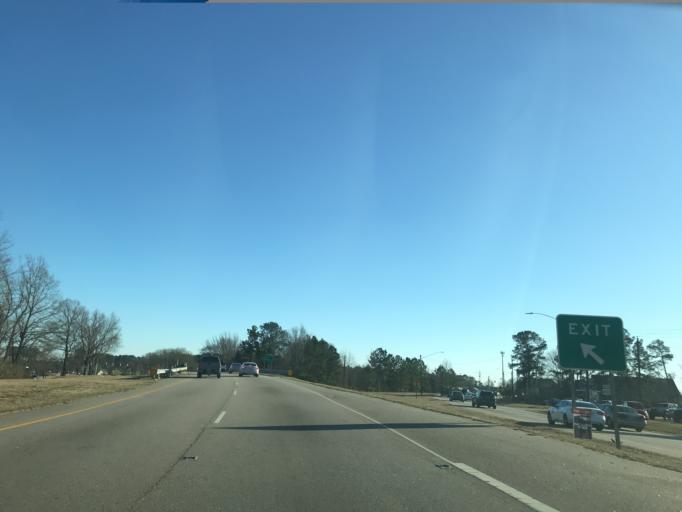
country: US
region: North Carolina
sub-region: Wake County
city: Garner
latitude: 35.7279
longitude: -78.6506
